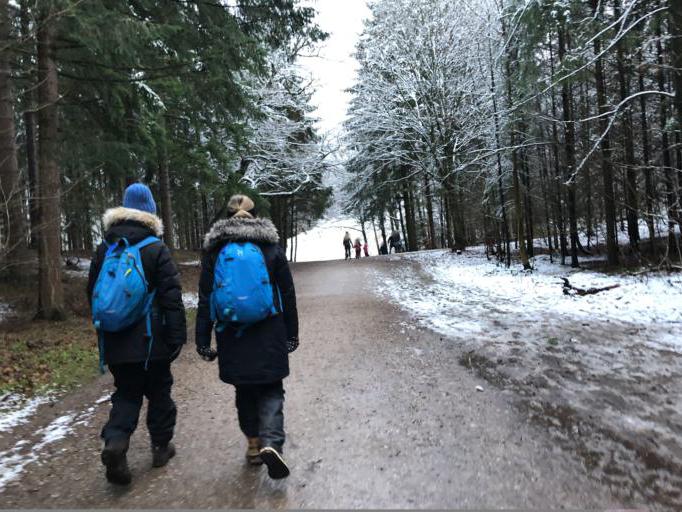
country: DK
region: Capital Region
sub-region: Rudersdal Kommune
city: Holte
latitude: 55.8077
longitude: 12.4838
